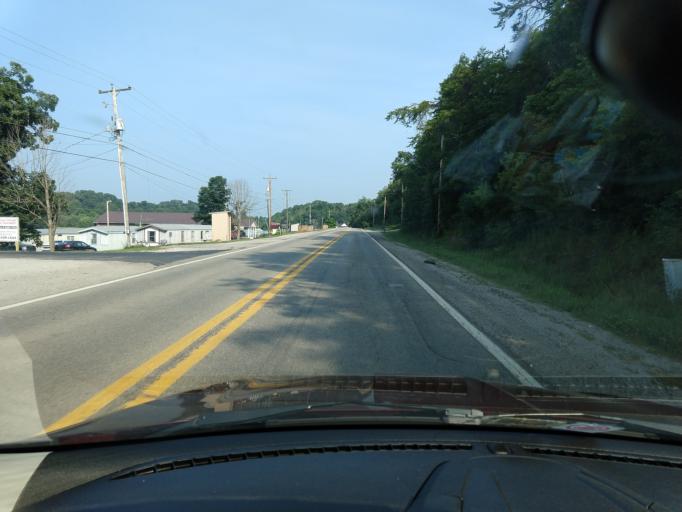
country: US
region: West Virginia
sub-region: Jackson County
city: Ripley
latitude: 38.8224
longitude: -81.7444
